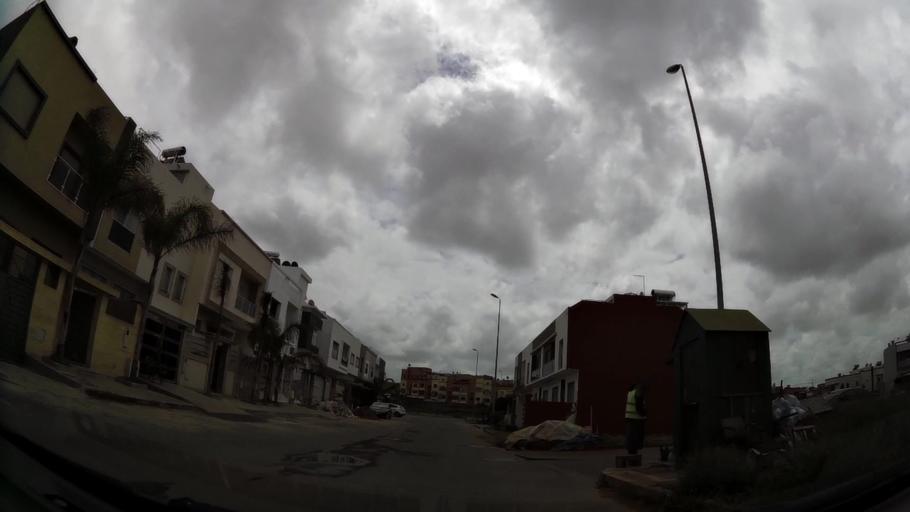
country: MA
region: Grand Casablanca
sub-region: Casablanca
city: Casablanca
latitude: 33.5310
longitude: -7.5969
